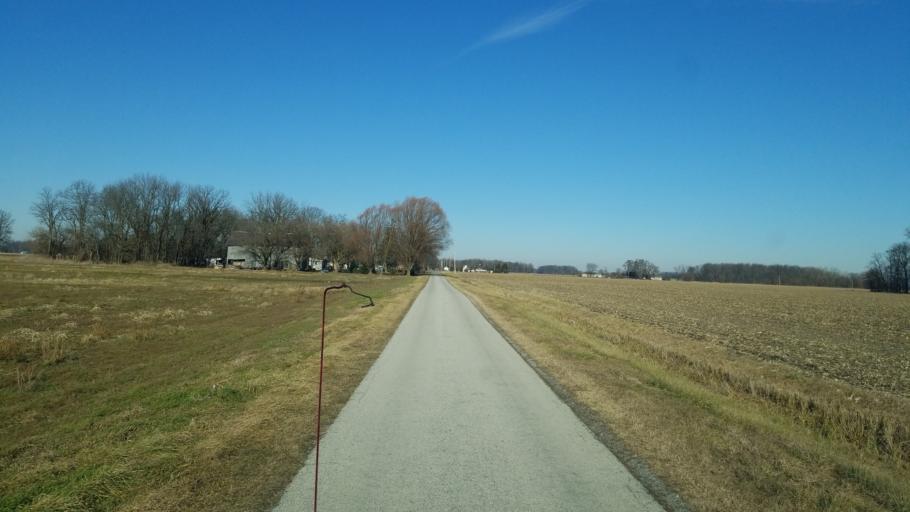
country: US
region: Ohio
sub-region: Henry County
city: Liberty Center
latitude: 41.3645
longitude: -83.9802
